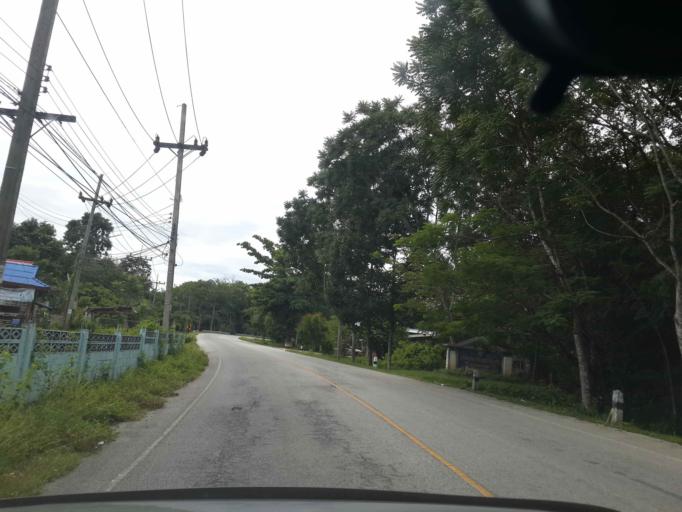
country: TH
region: Narathiwat
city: Rueso
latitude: 6.3831
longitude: 101.5164
